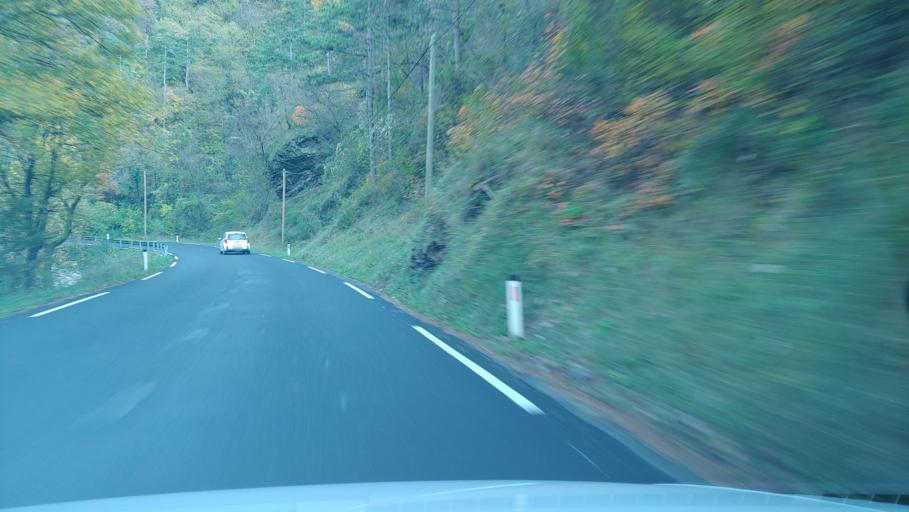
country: SI
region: Ajdovscina
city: Ajdovscina
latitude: 45.8097
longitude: 13.8747
